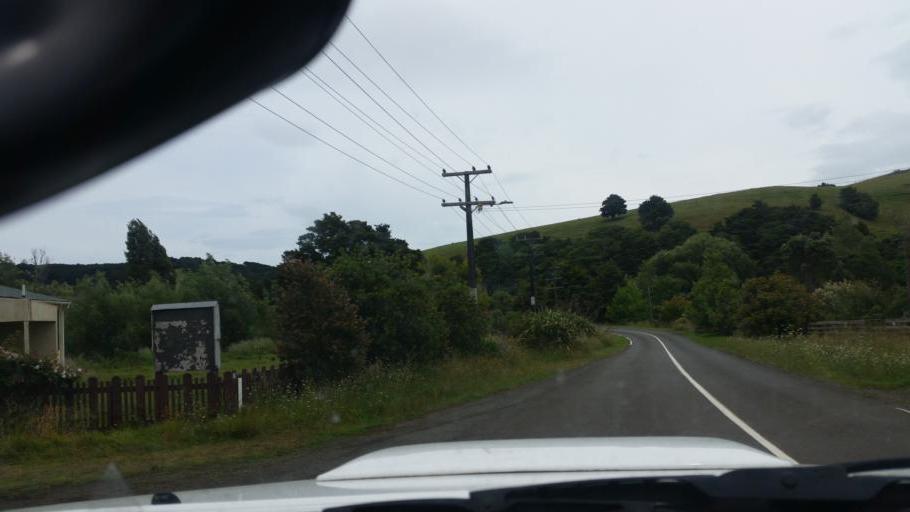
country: NZ
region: Northland
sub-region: Kaipara District
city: Dargaville
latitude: -35.7099
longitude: 173.6207
